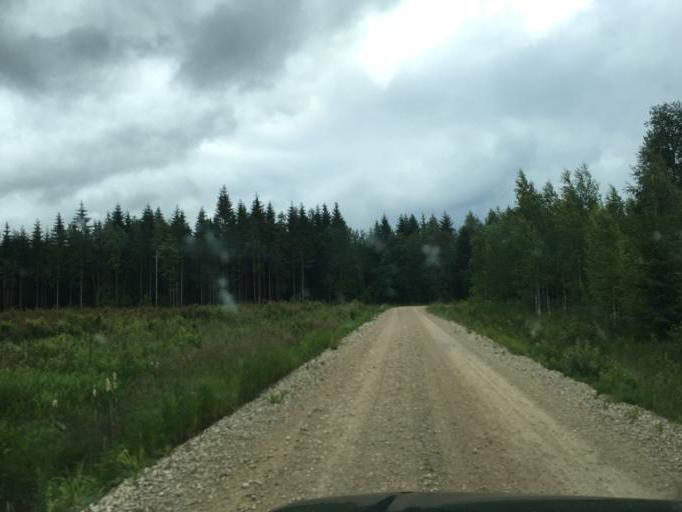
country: LV
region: Vilaka
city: Vilaka
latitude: 57.3875
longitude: 27.5183
